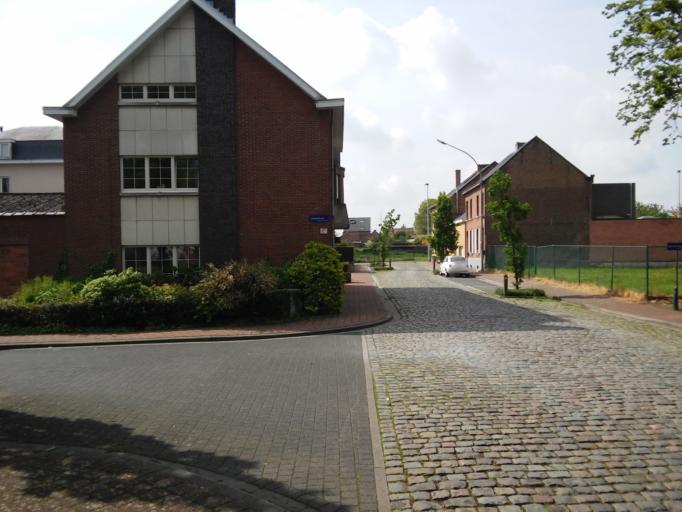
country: BE
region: Flanders
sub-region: Provincie Vlaams-Brabant
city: Zemst
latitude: 51.0147
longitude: 4.4409
